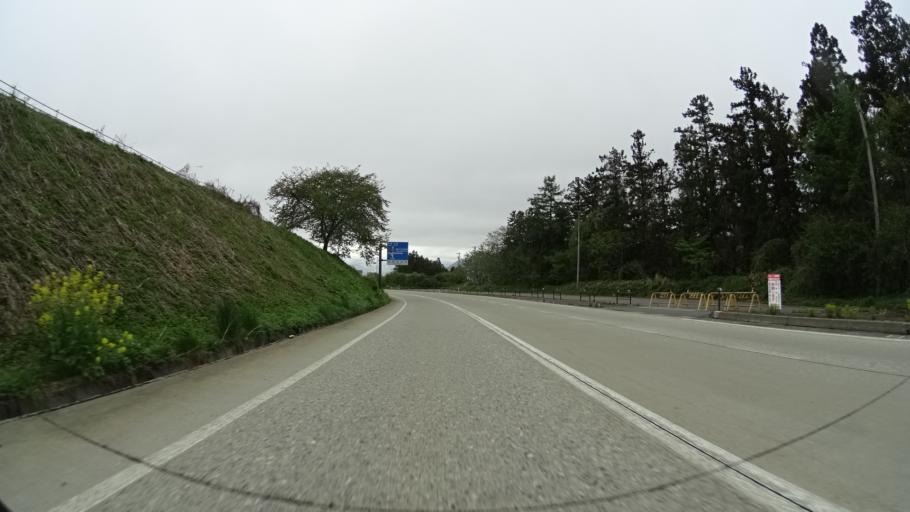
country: JP
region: Nagano
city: Nakano
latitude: 36.7330
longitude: 138.4202
